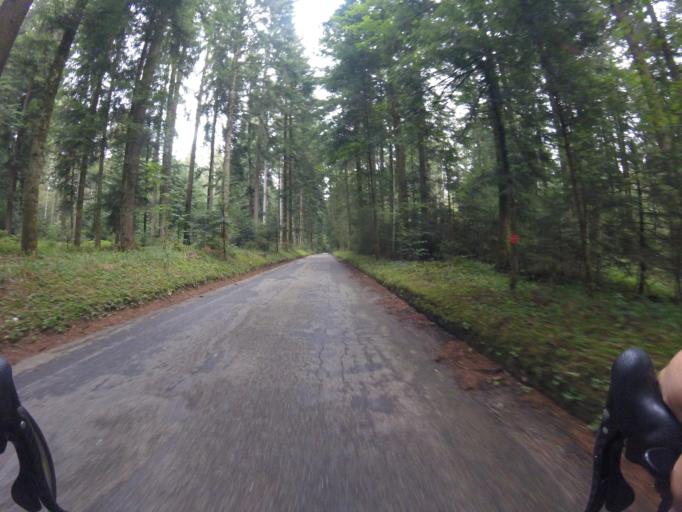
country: CH
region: Bern
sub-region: Bern-Mittelland District
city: Walkringen
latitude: 46.9559
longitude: 7.6485
